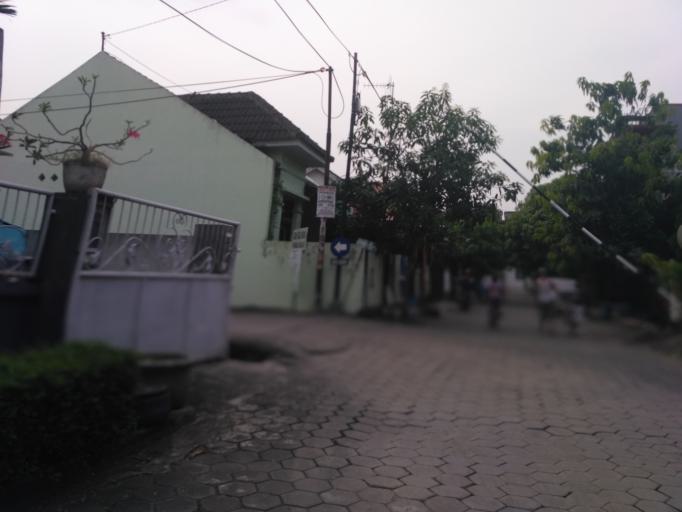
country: ID
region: Central Java
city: Mranggen
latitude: -7.0410
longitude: 110.4695
